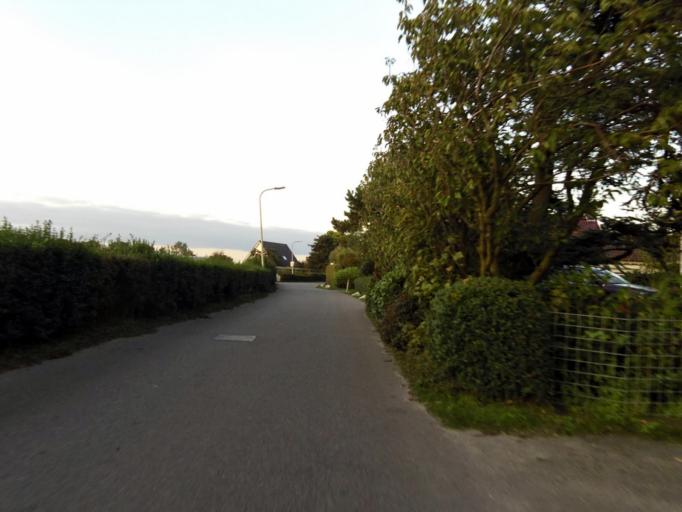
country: NL
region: South Holland
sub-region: Gemeente Wassenaar
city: Wassenaar
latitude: 52.1543
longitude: 4.4020
